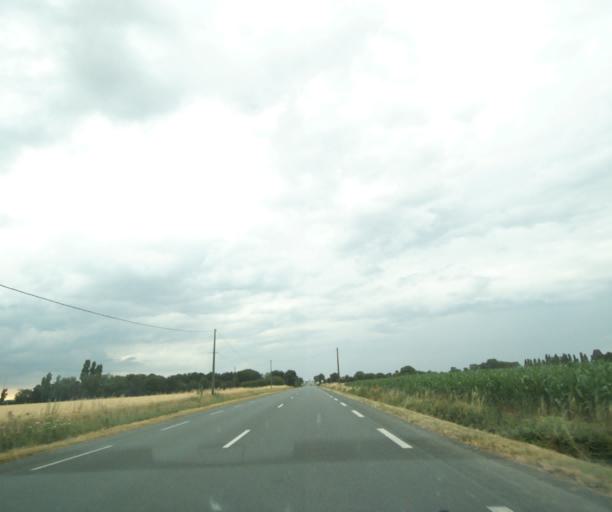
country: FR
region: Pays de la Loire
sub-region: Departement de la Vendee
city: Sainte-Gemme-la-Plaine
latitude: 46.4589
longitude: -1.1062
